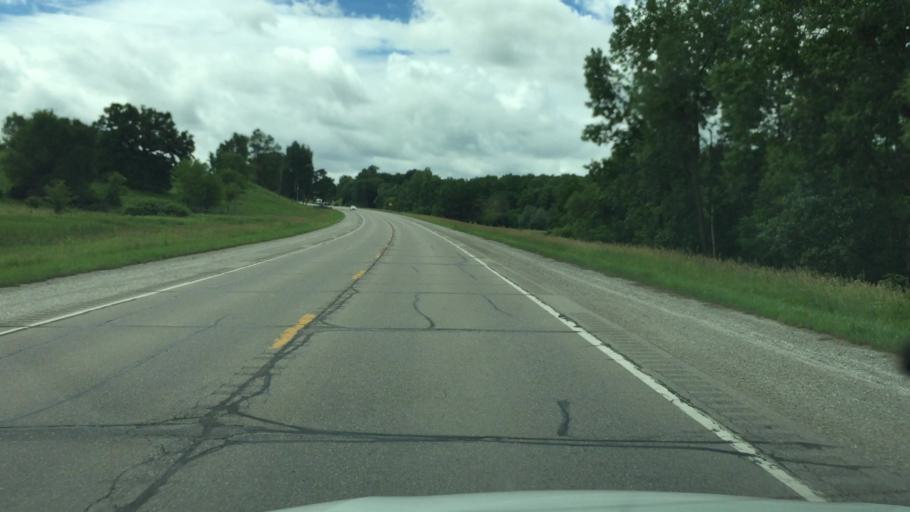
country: US
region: Iowa
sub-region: Jasper County
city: Monroe
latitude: 41.5349
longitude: -93.1016
